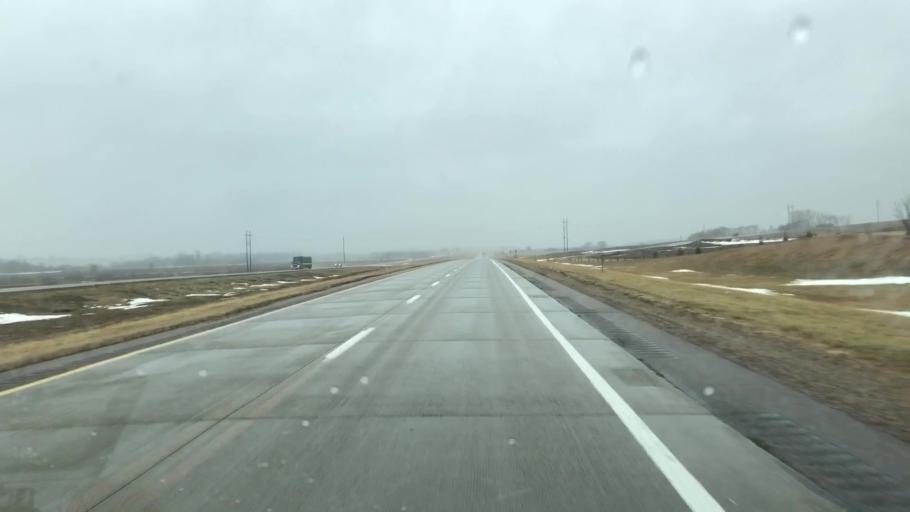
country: US
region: Iowa
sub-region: Sioux County
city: Orange City
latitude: 42.8983
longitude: -96.0879
